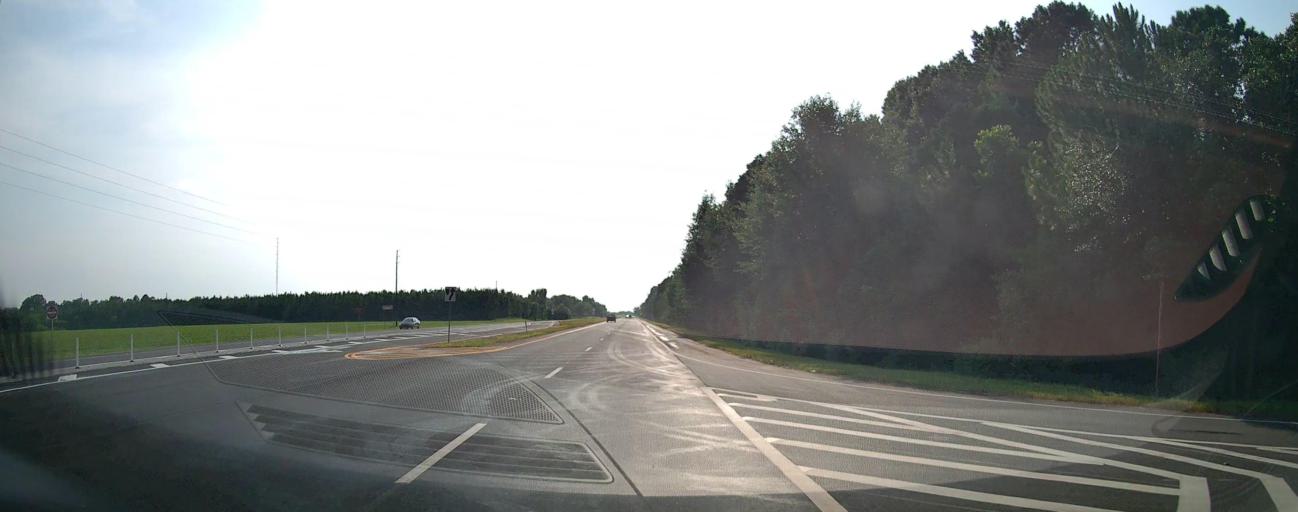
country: US
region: Georgia
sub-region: Peach County
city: Fort Valley
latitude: 32.5779
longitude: -83.8931
